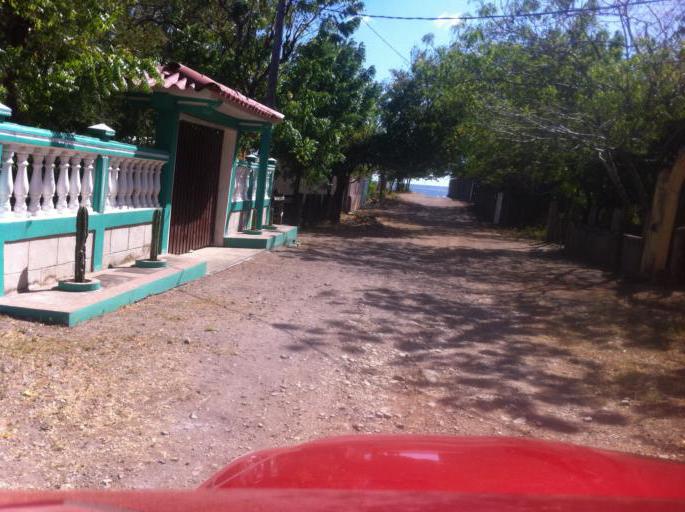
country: NI
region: Carazo
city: Santa Teresa
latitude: 11.6064
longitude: -86.3010
